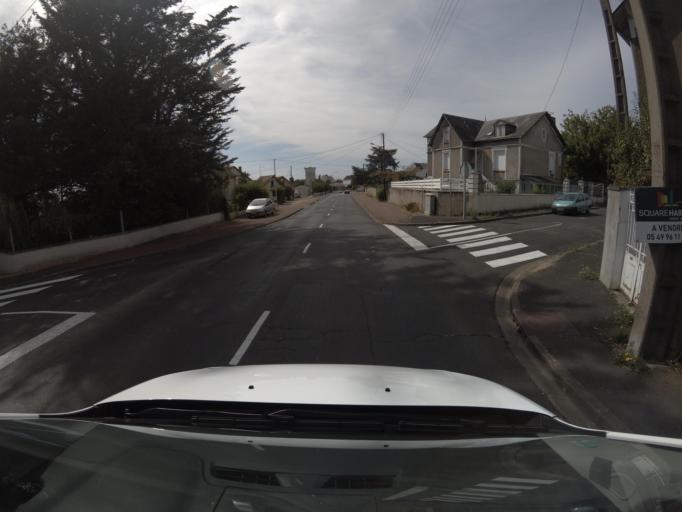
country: FR
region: Poitou-Charentes
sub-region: Departement des Deux-Sevres
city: Thouars
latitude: 46.9769
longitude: -0.2044
